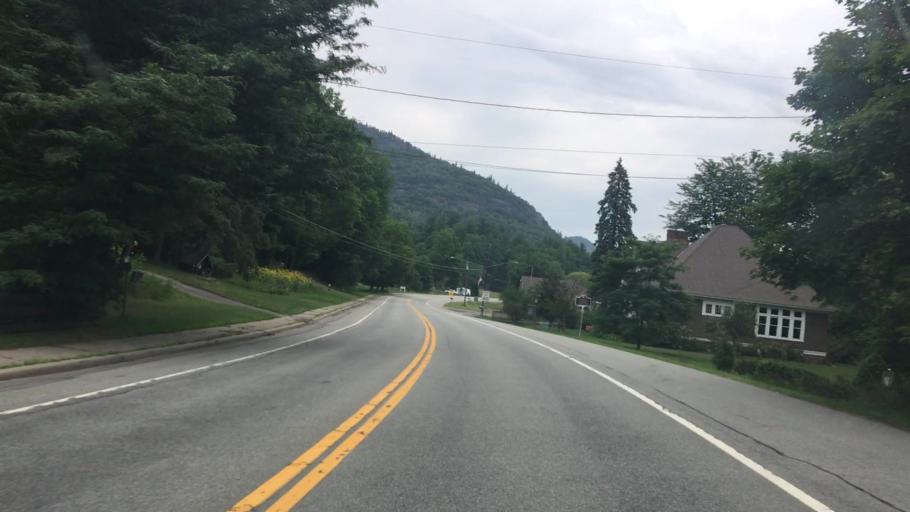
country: US
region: New York
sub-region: Essex County
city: Lake Placid
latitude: 44.3377
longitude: -73.7741
